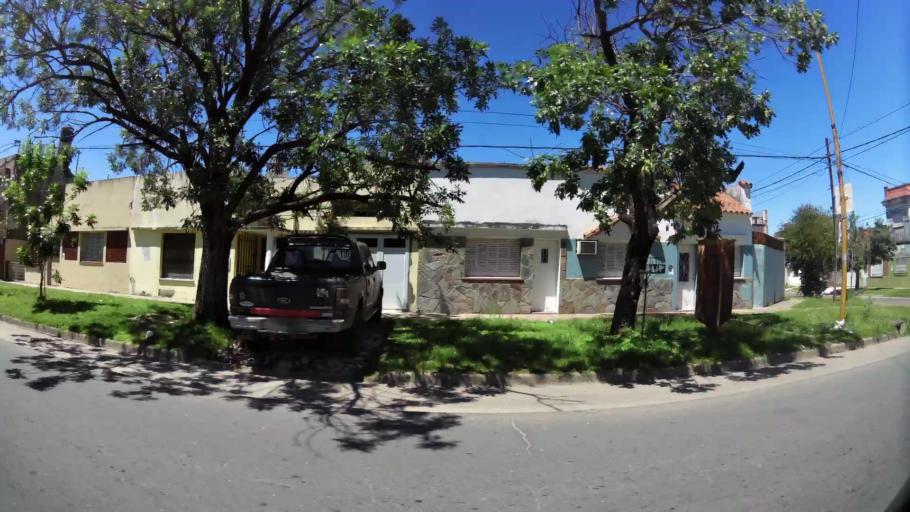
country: AR
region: Santa Fe
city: Santa Fe de la Vera Cruz
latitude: -31.6157
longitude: -60.7084
